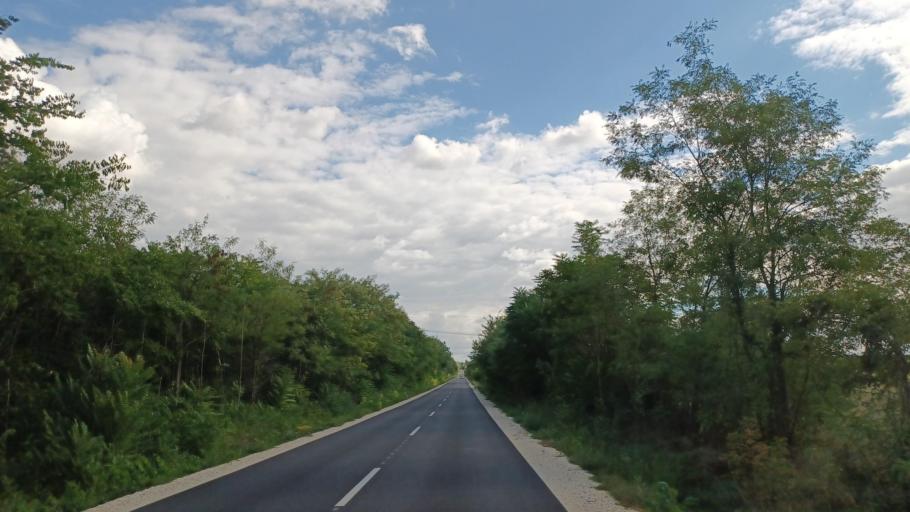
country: HU
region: Tolna
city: Nagydorog
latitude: 46.6092
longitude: 18.6866
